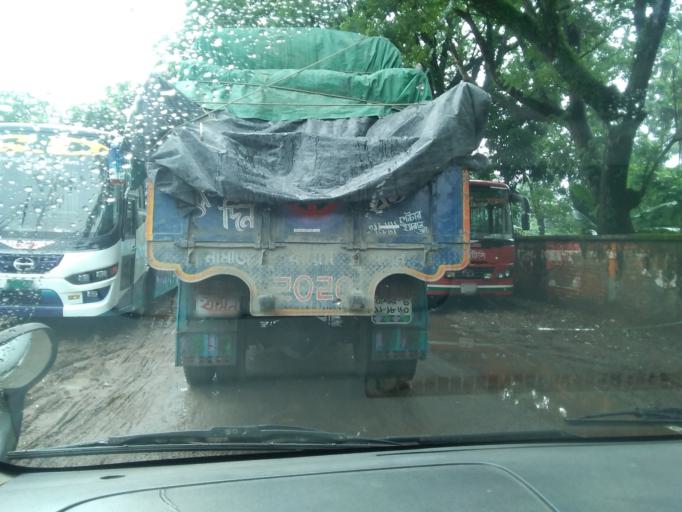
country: IN
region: West Bengal
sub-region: North 24 Parganas
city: Taki
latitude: 22.3459
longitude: 89.1042
